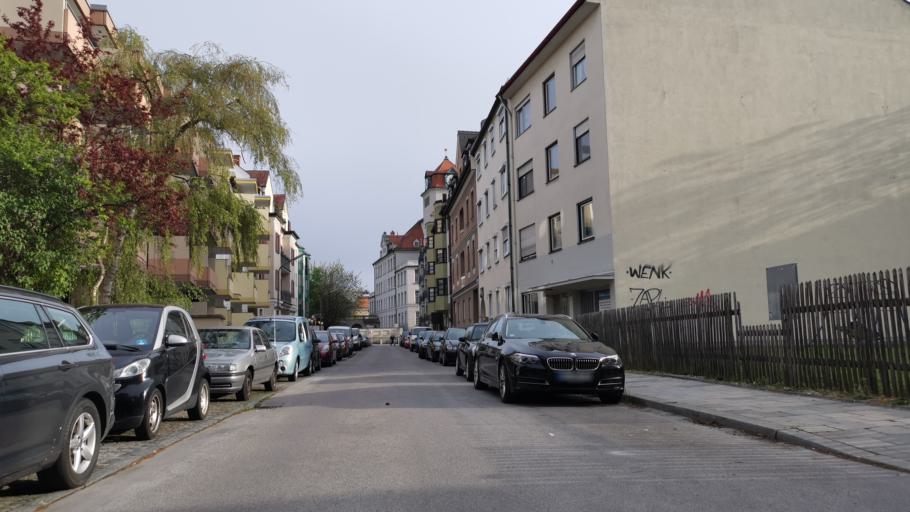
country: DE
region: Bavaria
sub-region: Upper Bavaria
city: Pullach im Isartal
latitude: 48.1014
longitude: 11.5367
